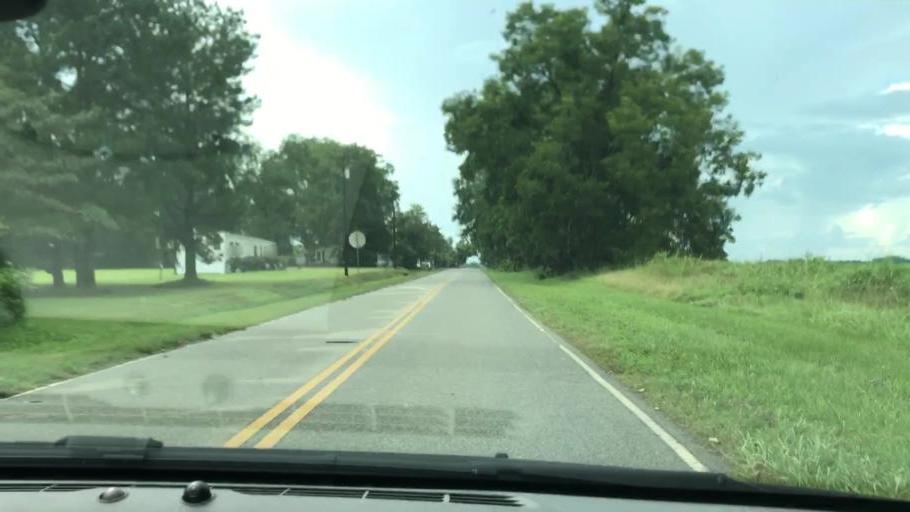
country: US
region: Georgia
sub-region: Early County
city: Blakely
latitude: 31.3748
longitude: -84.9518
